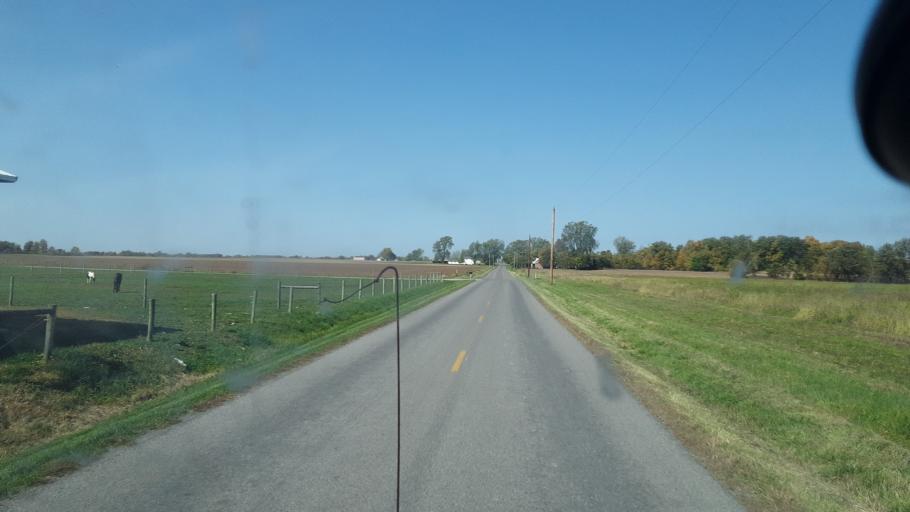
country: US
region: Ohio
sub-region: Logan County
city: Northwood
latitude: 40.4997
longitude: -83.7829
